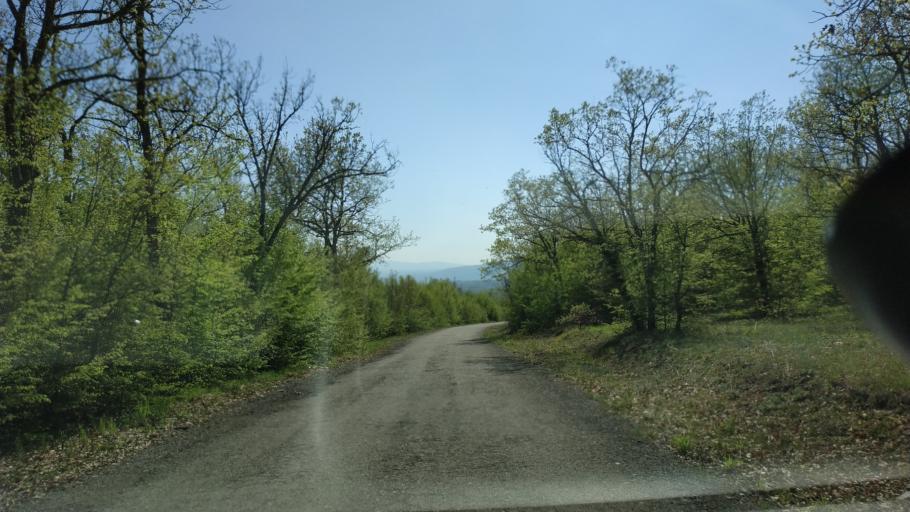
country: RS
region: Central Serbia
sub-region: Zajecarski Okrug
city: Soko Banja
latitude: 43.5025
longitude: 21.8883
